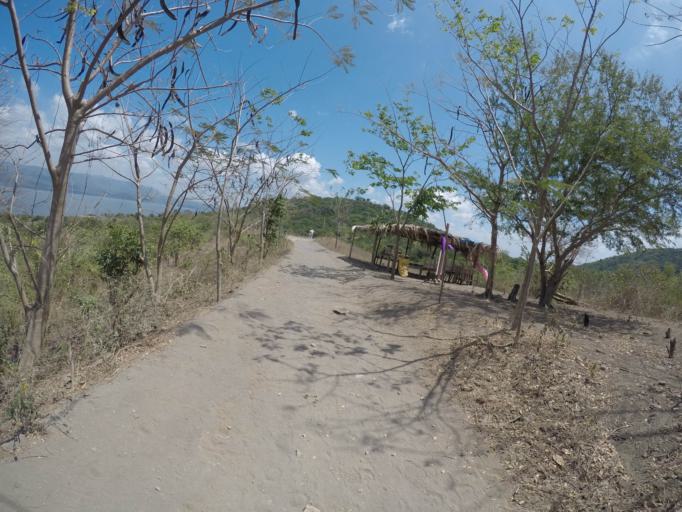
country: PH
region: Calabarzon
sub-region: Province of Batangas
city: Bugaan
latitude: 14.0249
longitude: 120.9995
